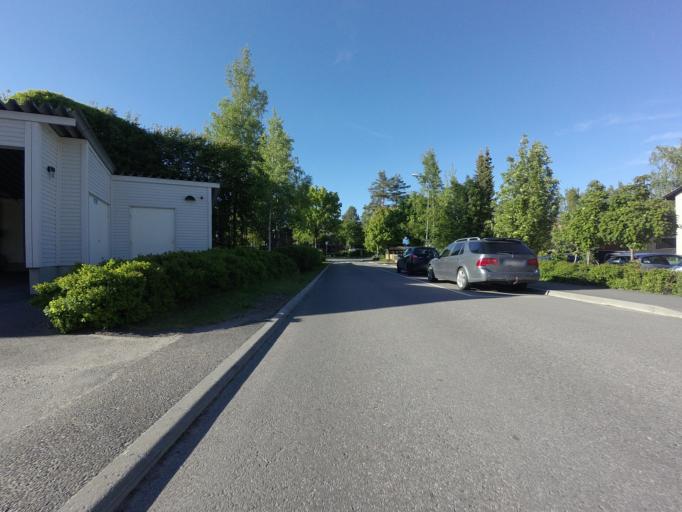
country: FI
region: Uusimaa
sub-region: Helsinki
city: Koukkuniemi
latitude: 60.1712
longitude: 24.7444
